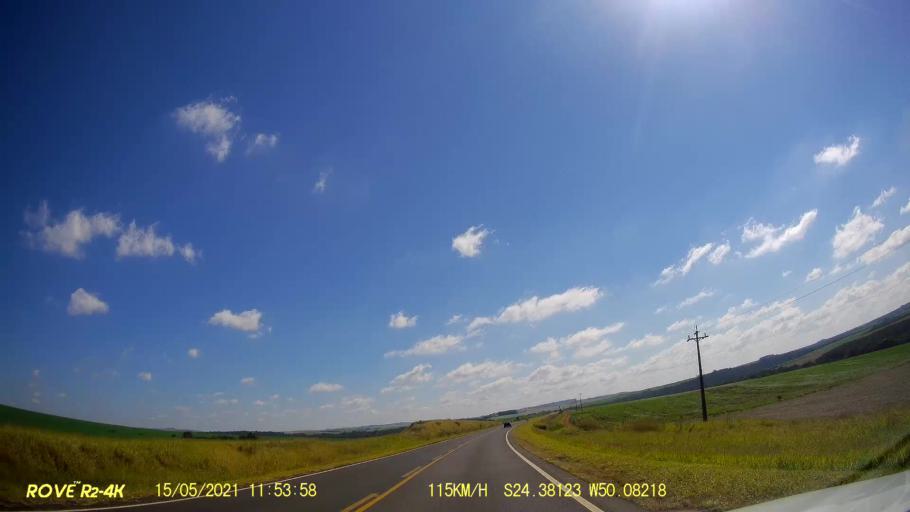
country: BR
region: Parana
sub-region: Pirai Do Sul
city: Pirai do Sul
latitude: -24.3823
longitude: -50.0815
